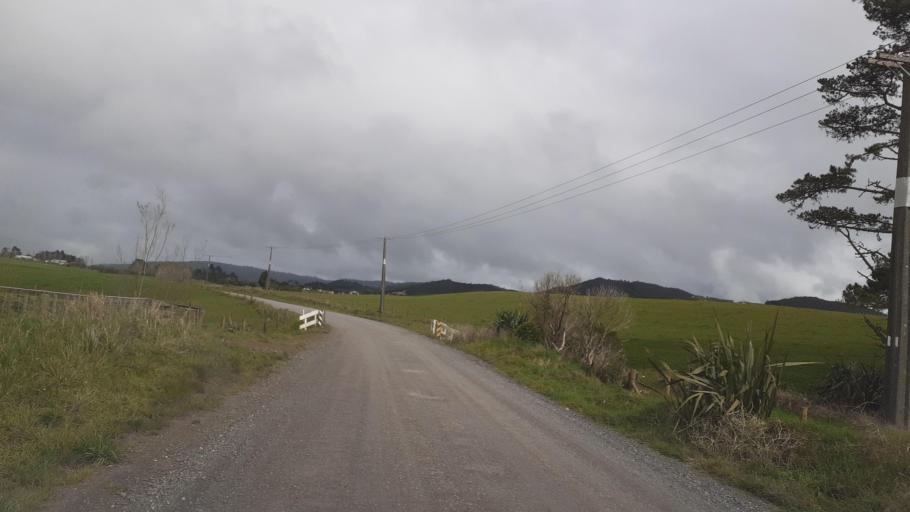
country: NZ
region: Northland
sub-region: Far North District
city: Waimate North
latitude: -35.2433
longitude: 173.8066
